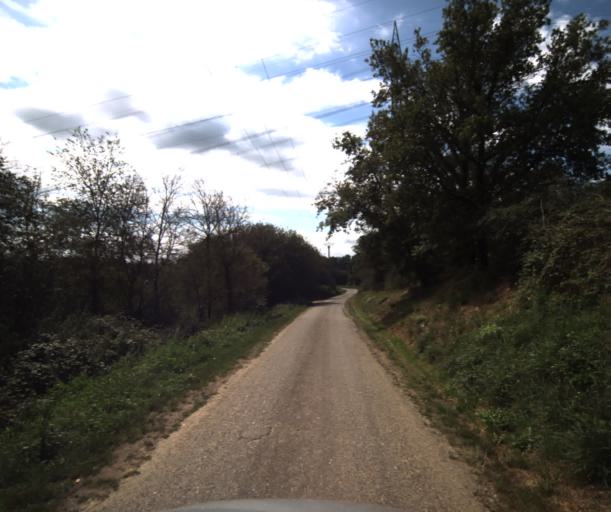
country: FR
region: Midi-Pyrenees
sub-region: Departement de la Haute-Garonne
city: Lacasse
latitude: 43.3801
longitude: 1.2561
